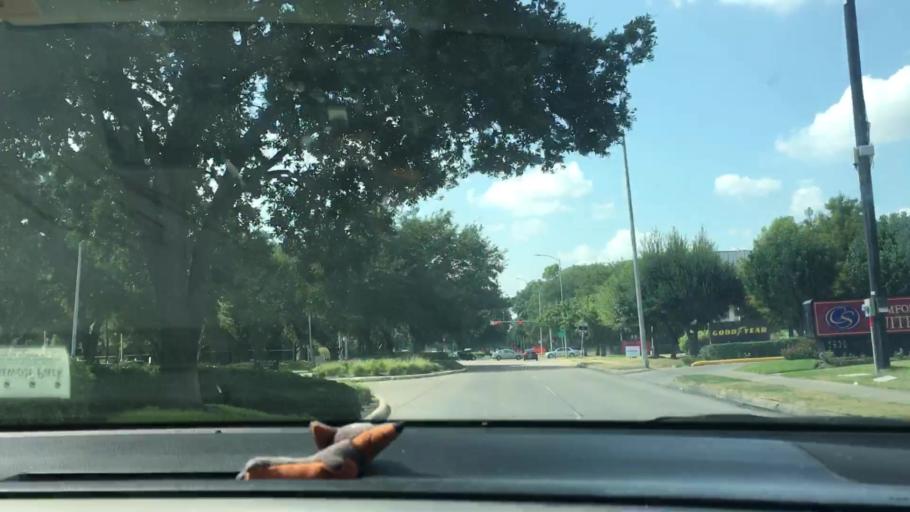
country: US
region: Texas
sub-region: Harris County
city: Bunker Hill Village
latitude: 29.7341
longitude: -95.5719
